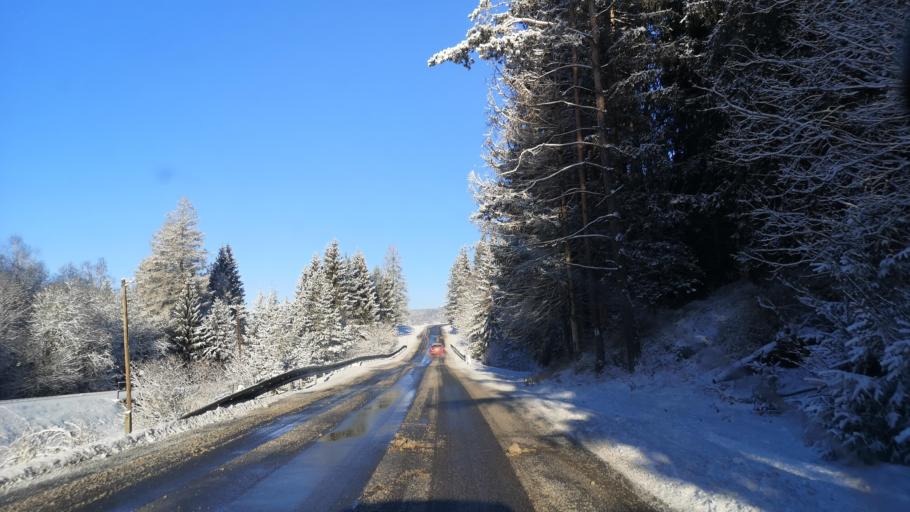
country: SK
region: Banskobystricky
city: Revuca
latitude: 48.8283
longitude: 20.1232
